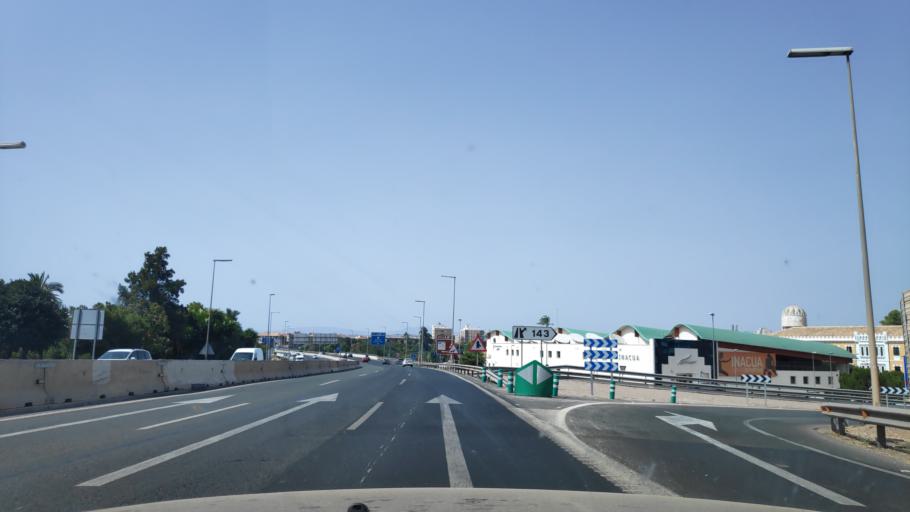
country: ES
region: Murcia
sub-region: Murcia
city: Murcia
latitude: 37.9766
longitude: -1.1363
